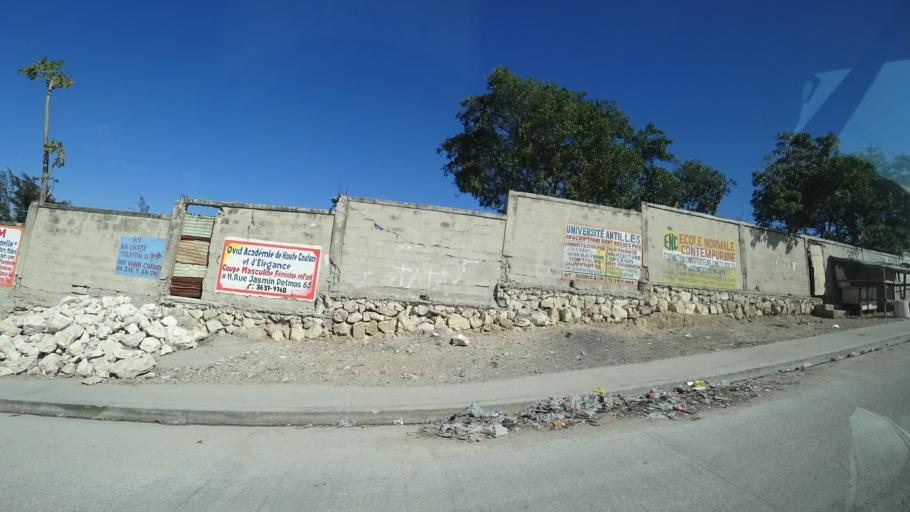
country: HT
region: Ouest
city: Delmas 73
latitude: 18.5637
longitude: -72.2878
